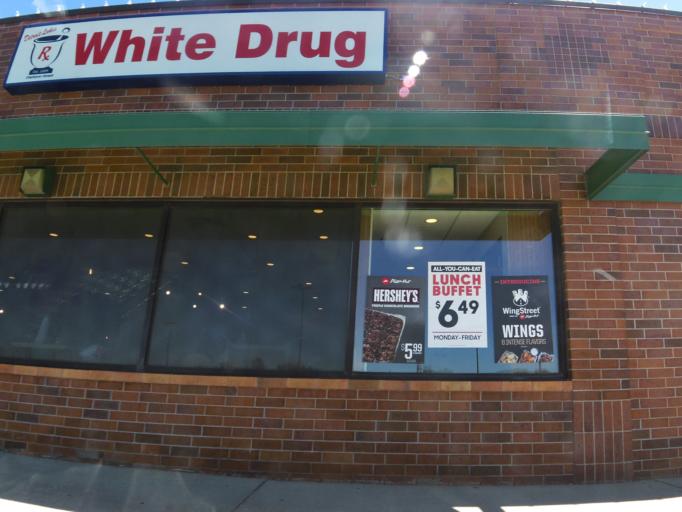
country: US
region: Minnesota
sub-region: Becker County
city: Detroit Lakes
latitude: 46.8180
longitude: -95.8469
